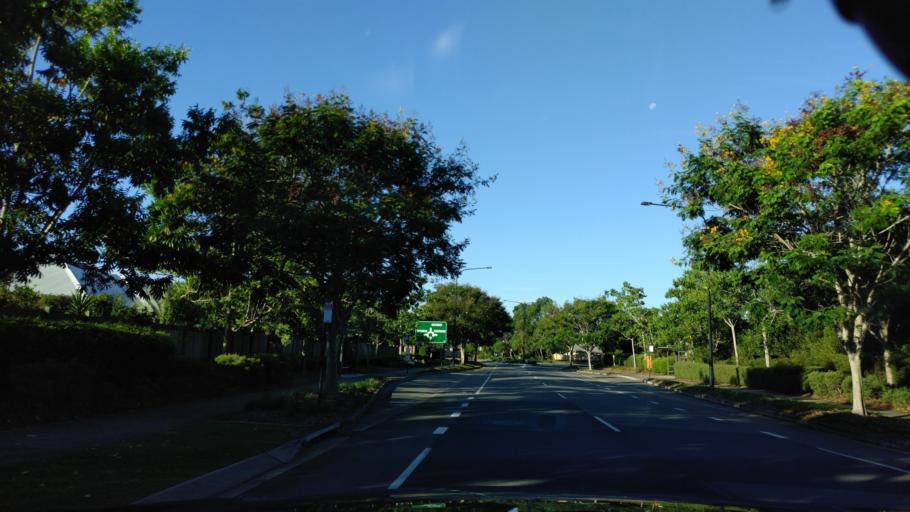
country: AU
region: Queensland
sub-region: Moreton Bay
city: Deception Bay
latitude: -27.2134
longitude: 153.0237
